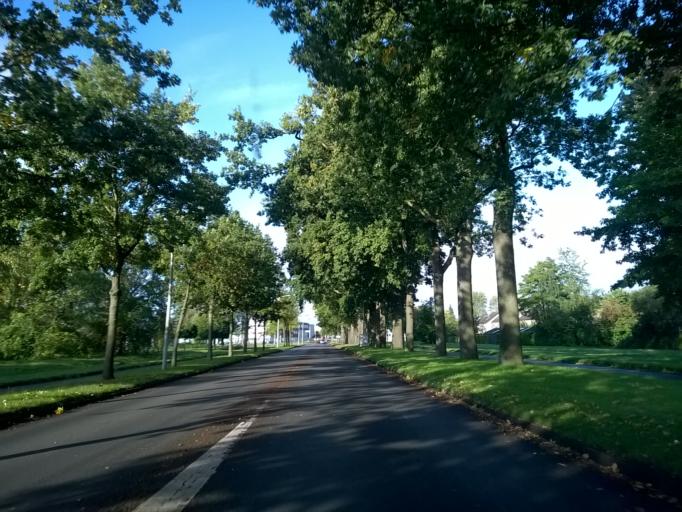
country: NL
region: Friesland
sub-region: Gemeente Smallingerland
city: Drachten
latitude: 53.1064
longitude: 6.1240
